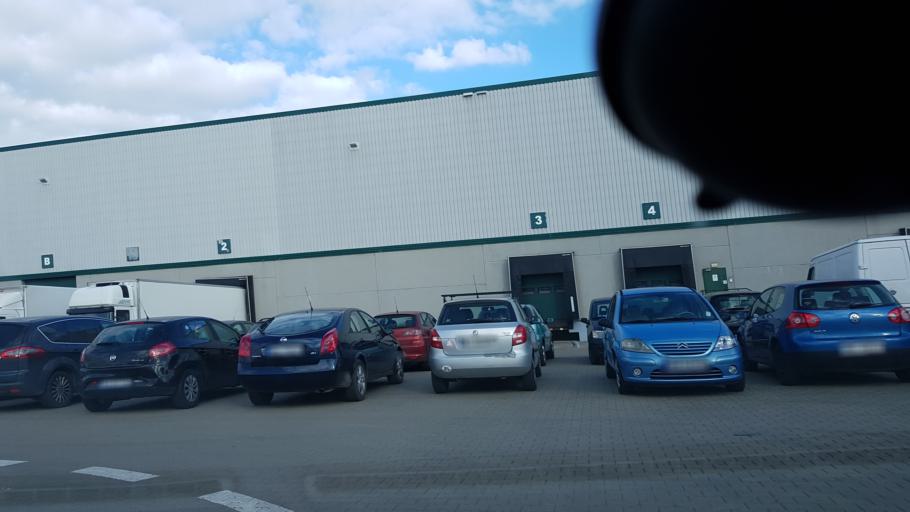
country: PL
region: Masovian Voivodeship
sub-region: Warszawa
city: Targowek
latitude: 52.3103
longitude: 21.0202
